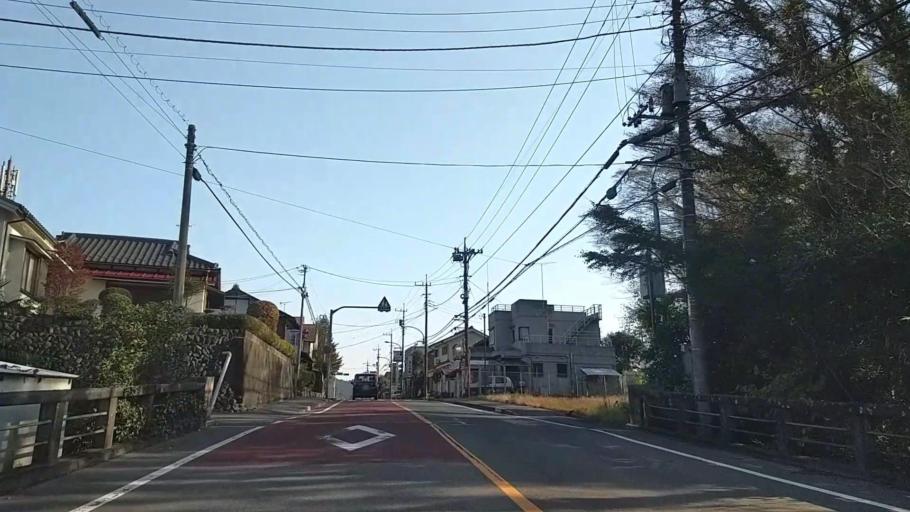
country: JP
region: Tokyo
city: Ome
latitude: 35.8051
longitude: 139.2144
